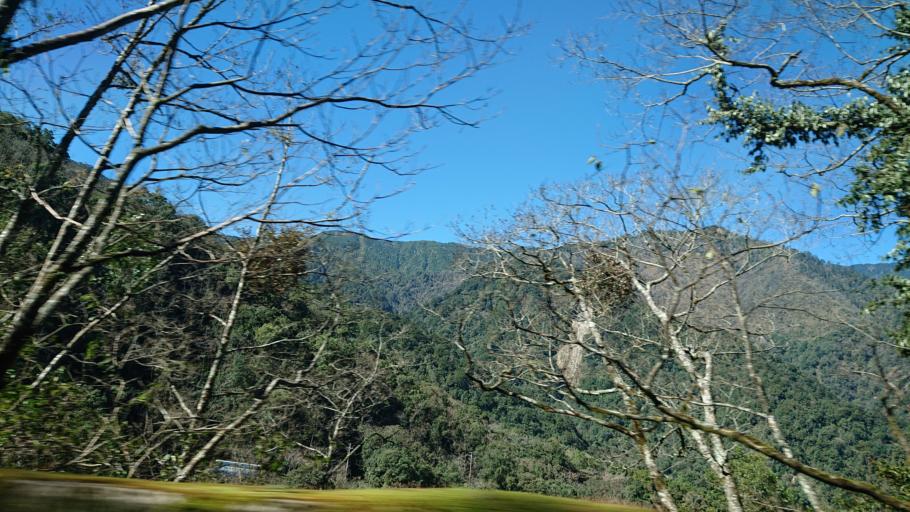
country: TW
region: Taiwan
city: Daxi
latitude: 24.4046
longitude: 121.3666
